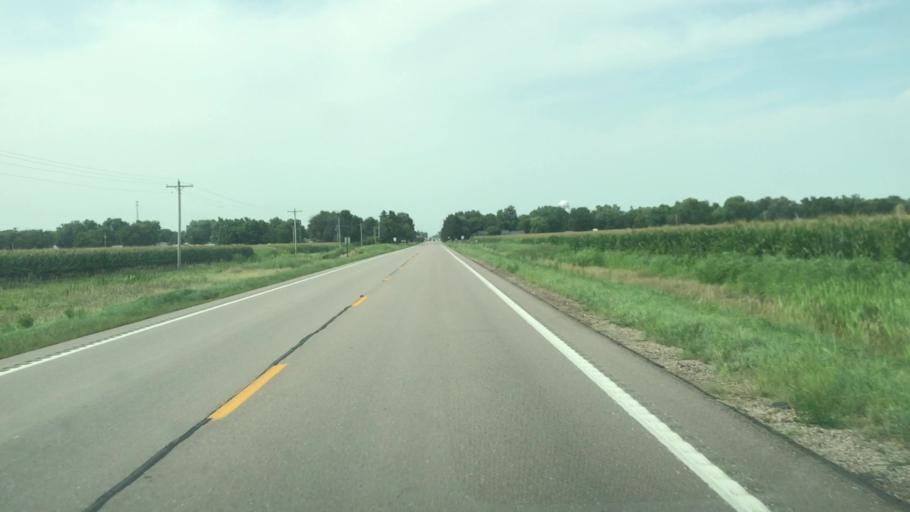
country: US
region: Nebraska
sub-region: Hall County
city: Wood River
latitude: 40.9927
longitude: -98.6075
